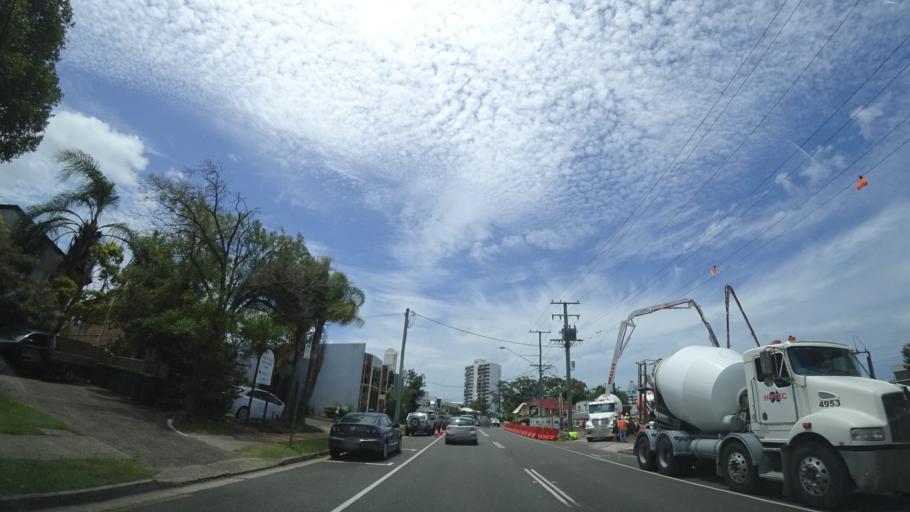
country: AU
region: Queensland
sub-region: Sunshine Coast
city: Mooloolaba
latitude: -26.6518
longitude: 153.0894
